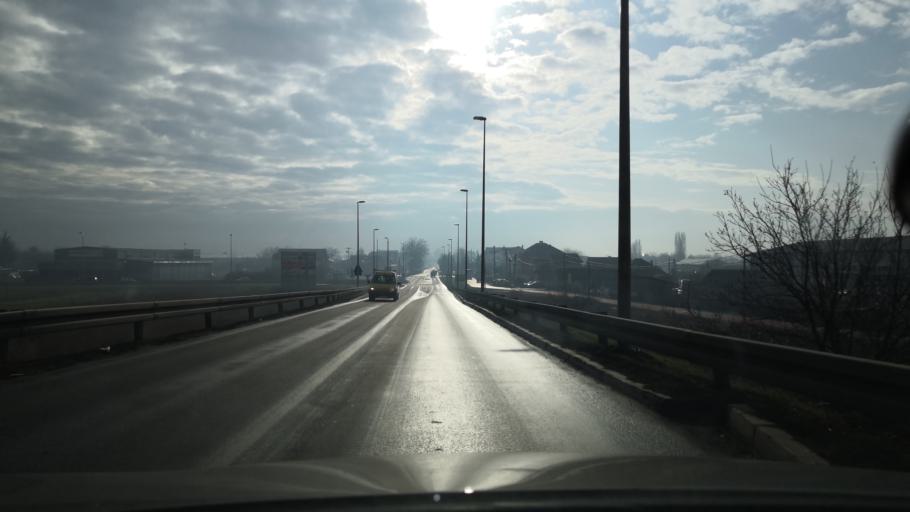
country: RS
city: Dobanovci
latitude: 44.8431
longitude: 20.2121
